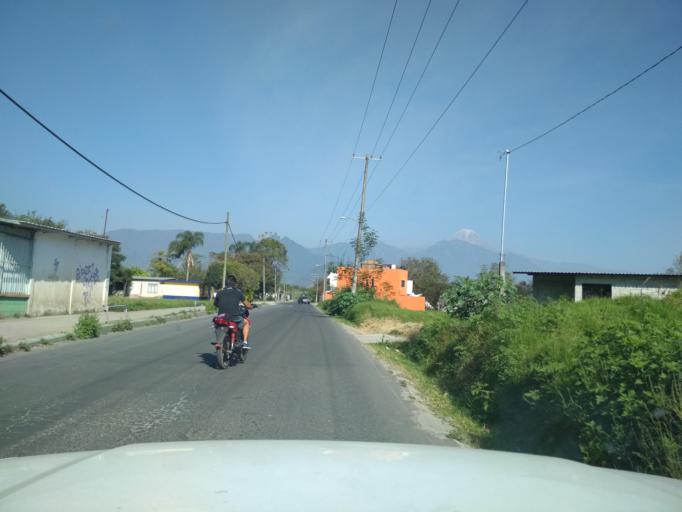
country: MX
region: Veracruz
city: Jalapilla
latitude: 18.8183
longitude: -97.0784
